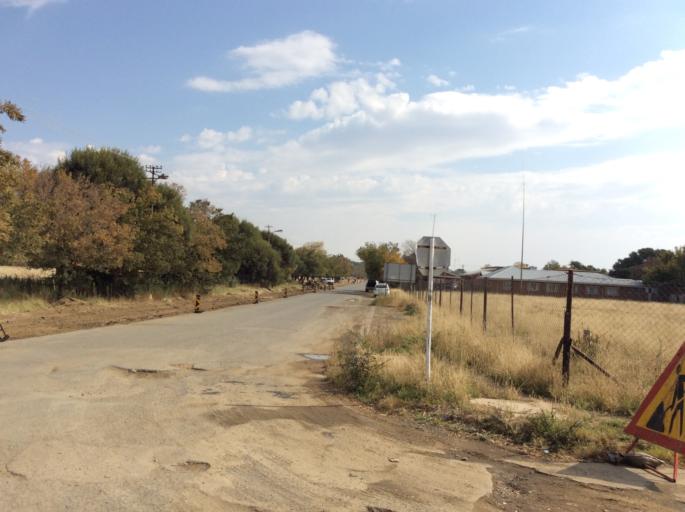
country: LS
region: Mafeteng
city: Mafeteng
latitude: -29.7314
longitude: 27.0387
